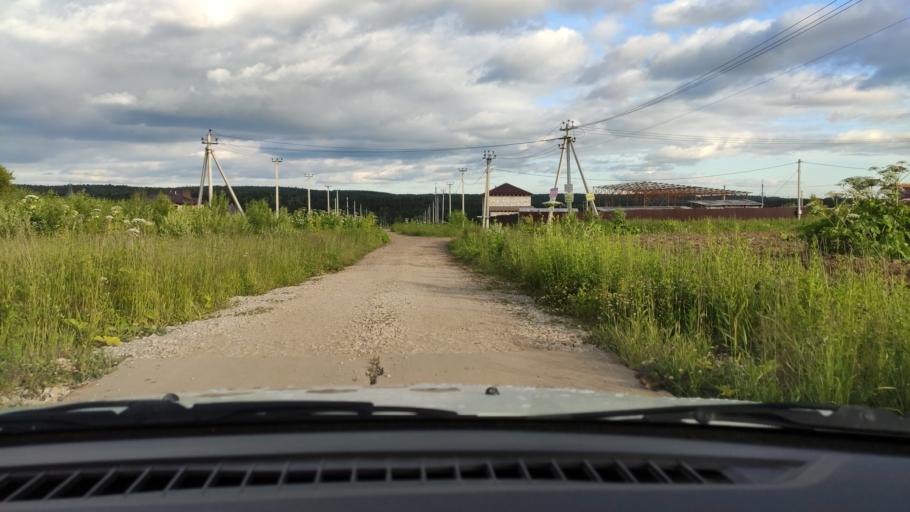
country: RU
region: Perm
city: Perm
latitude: 58.0356
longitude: 56.3793
